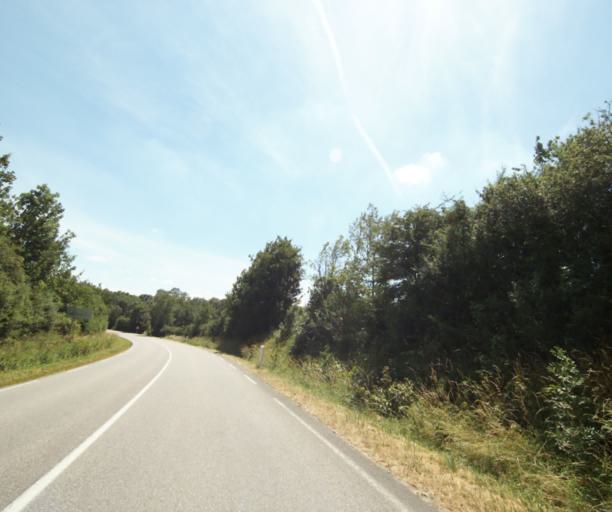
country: FR
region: Lorraine
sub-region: Departement de Meurthe-et-Moselle
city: Luneville
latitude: 48.6126
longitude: 6.4885
